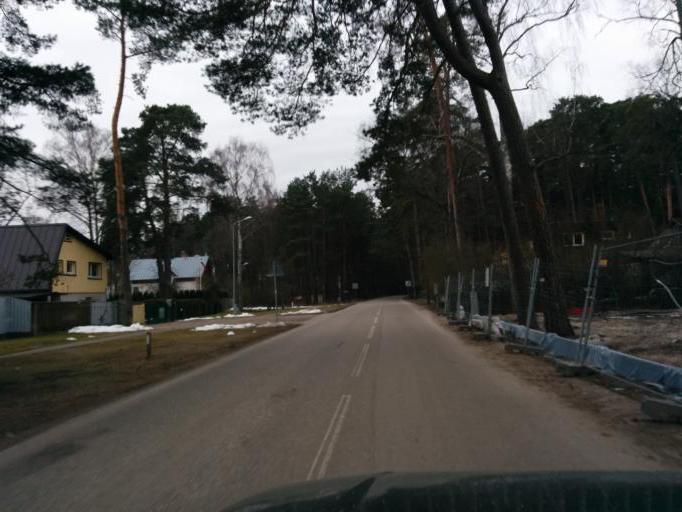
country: LV
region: Babite
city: Pinki
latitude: 56.9925
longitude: 23.9139
